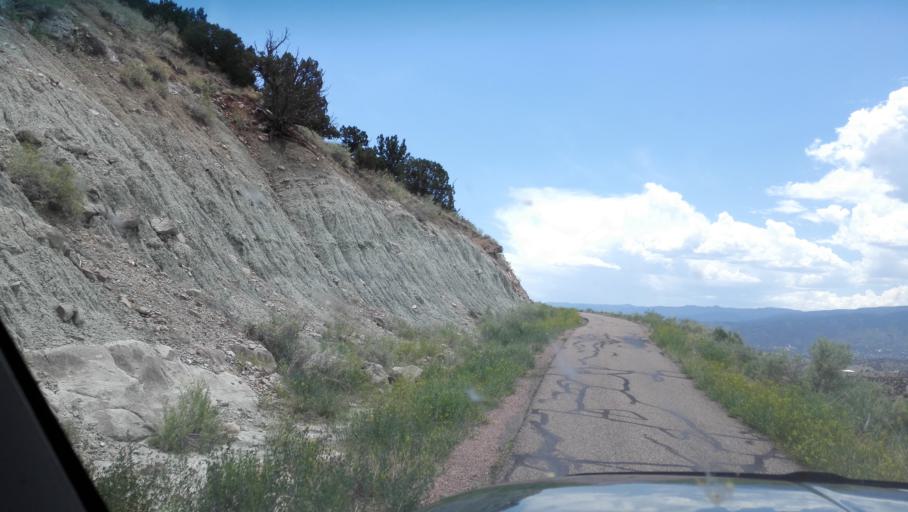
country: US
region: Colorado
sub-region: Fremont County
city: Canon City
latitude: 38.4702
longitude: -105.2555
